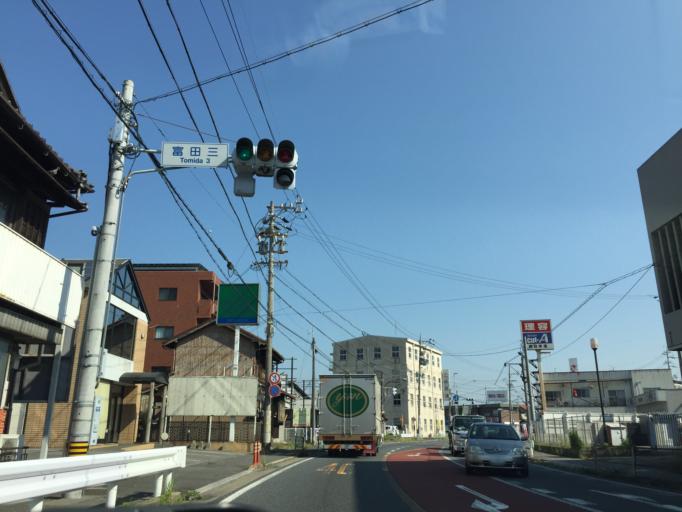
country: JP
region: Mie
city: Yokkaichi
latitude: 35.0067
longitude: 136.6544
